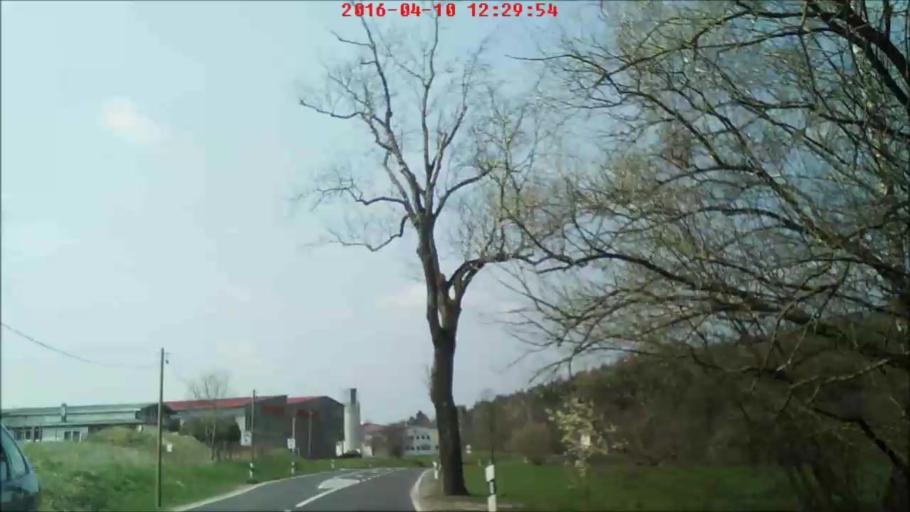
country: DE
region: Thuringia
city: Springstille
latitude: 50.6878
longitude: 10.5163
